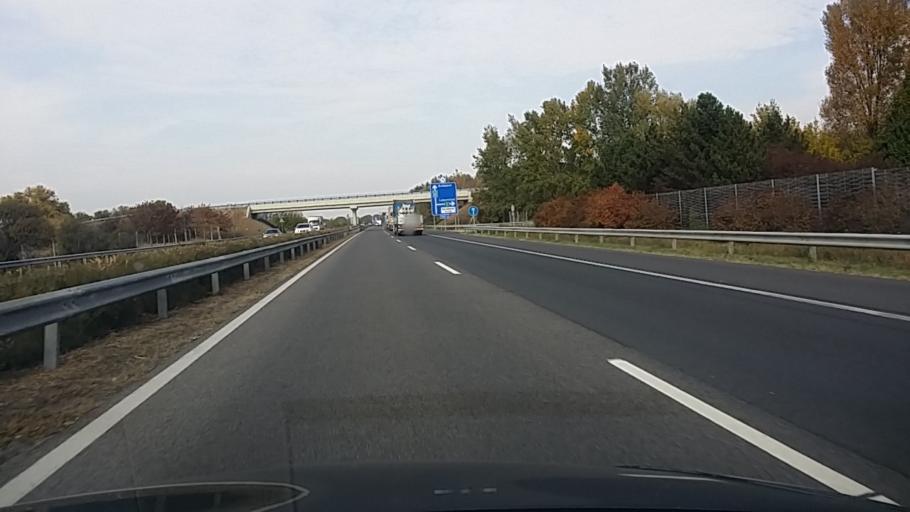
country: HU
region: Bacs-Kiskun
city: Lajosmizse
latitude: 46.9736
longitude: 19.6133
